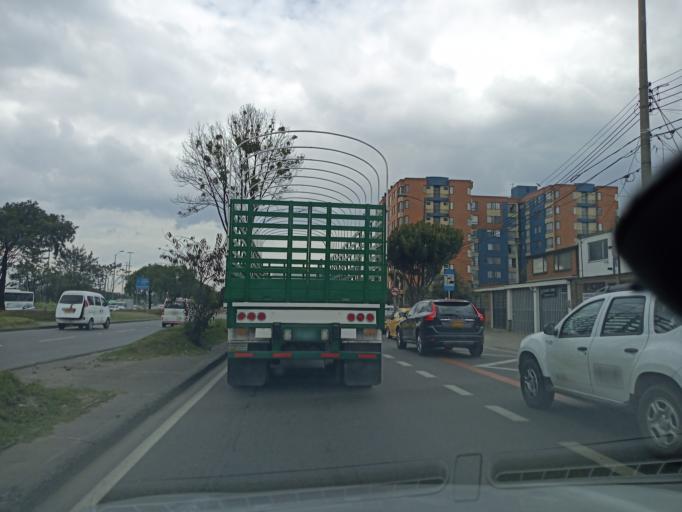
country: CO
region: Bogota D.C.
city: Bogota
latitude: 4.6270
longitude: -74.1375
